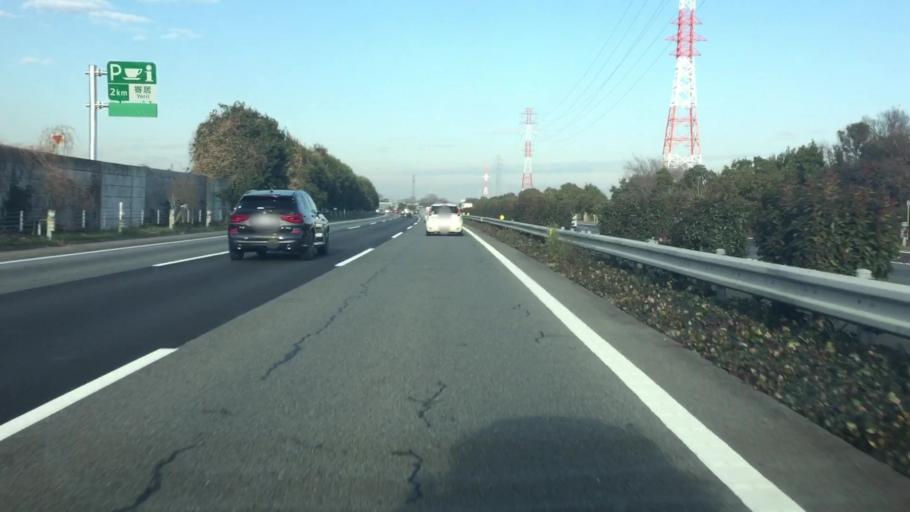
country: JP
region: Saitama
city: Yorii
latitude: 36.1588
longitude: 139.2122
